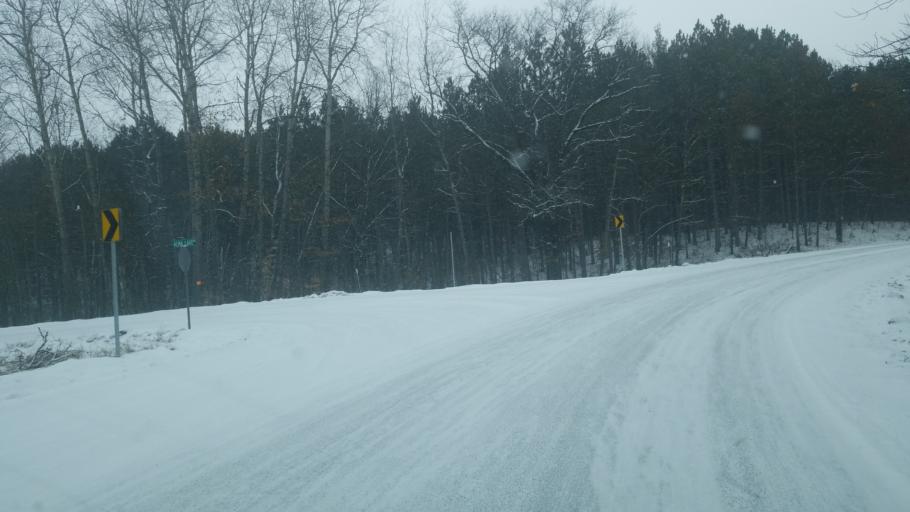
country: US
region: Michigan
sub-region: Mecosta County
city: Big Rapids
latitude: 43.7345
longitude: -85.4118
